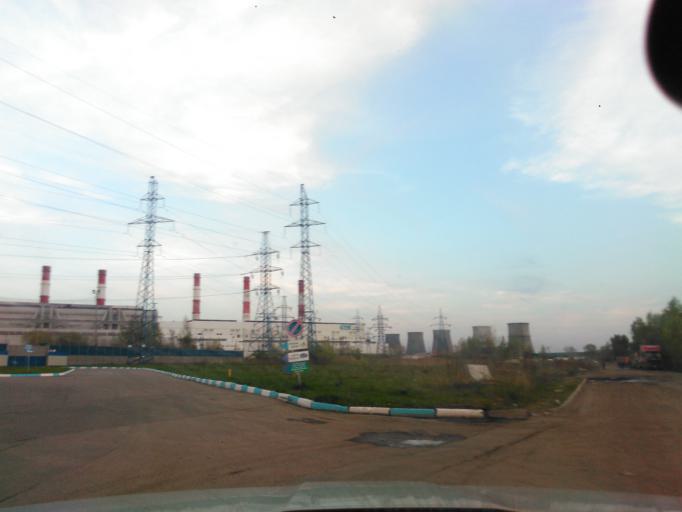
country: RU
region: Moskovskaya
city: Alekseyevka
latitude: 55.6392
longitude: 37.8110
